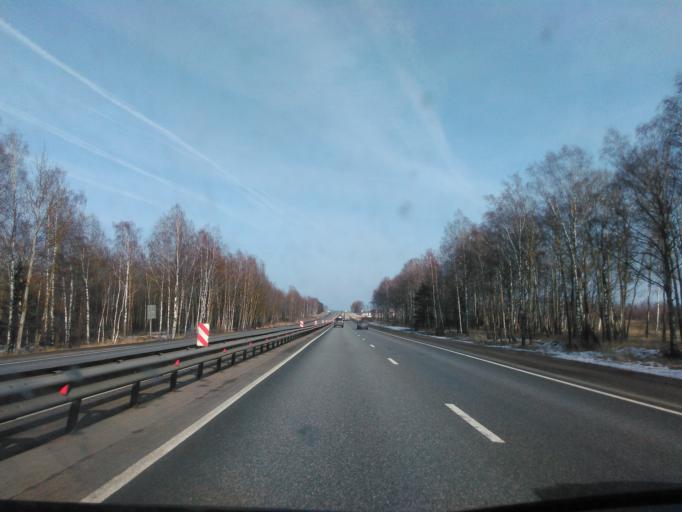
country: RU
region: Smolensk
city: Verkhnedneprovskiy
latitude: 55.1755
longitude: 33.4435
